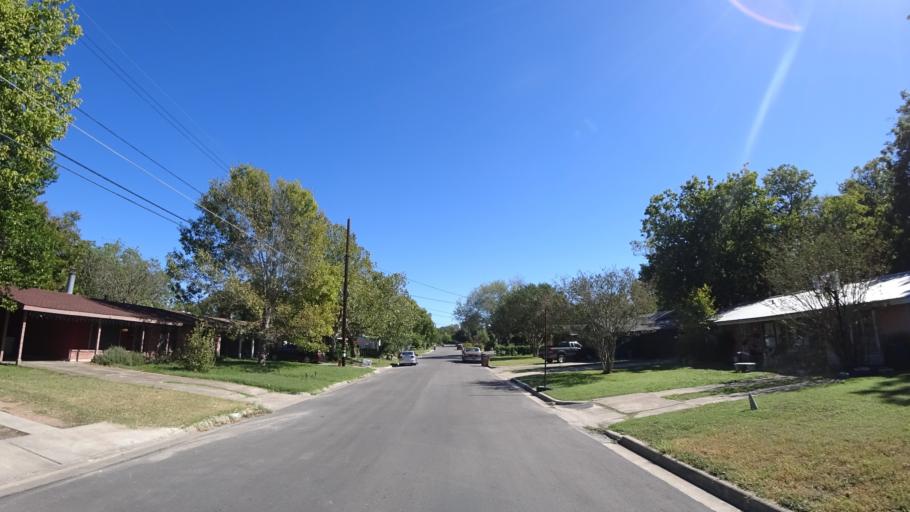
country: US
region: Texas
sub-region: Travis County
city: Austin
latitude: 30.3391
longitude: -97.7345
